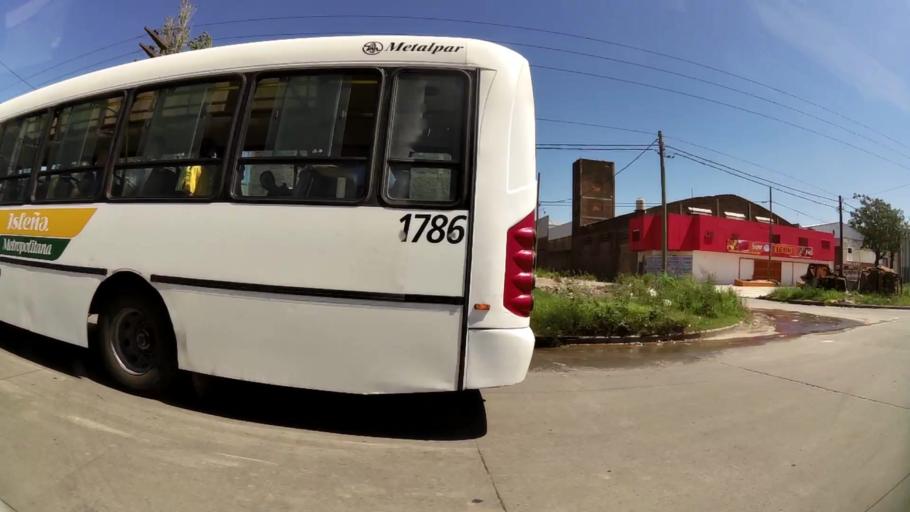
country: AR
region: Buenos Aires
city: Caseros
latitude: -34.5630
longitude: -58.5782
